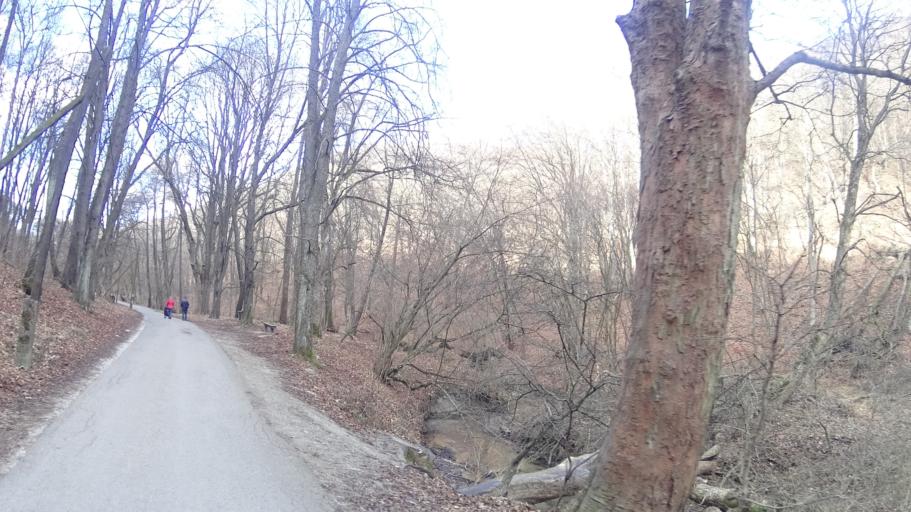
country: HU
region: Heves
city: Szilvasvarad
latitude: 48.0888
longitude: 20.4047
